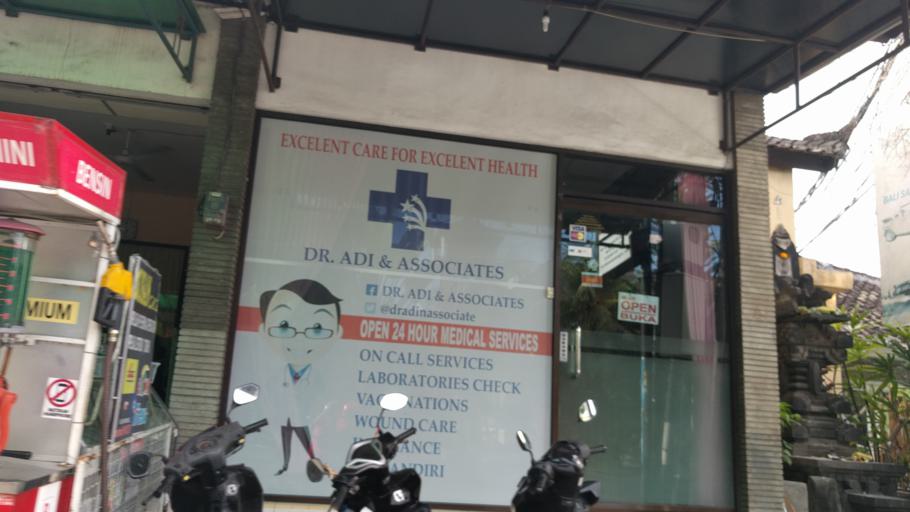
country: ID
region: Bali
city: Kuta
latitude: -8.6973
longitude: 115.1718
